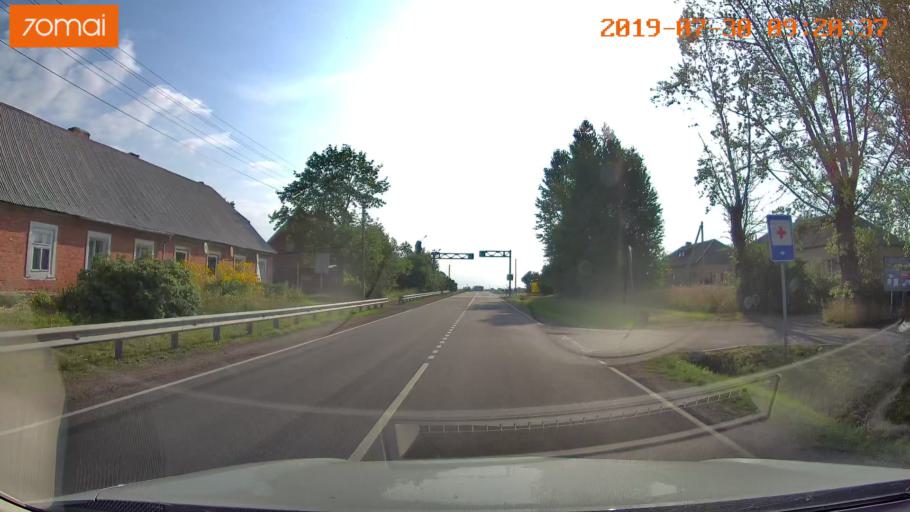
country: RU
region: Kaliningrad
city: Nesterov
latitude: 54.6358
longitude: 22.6139
